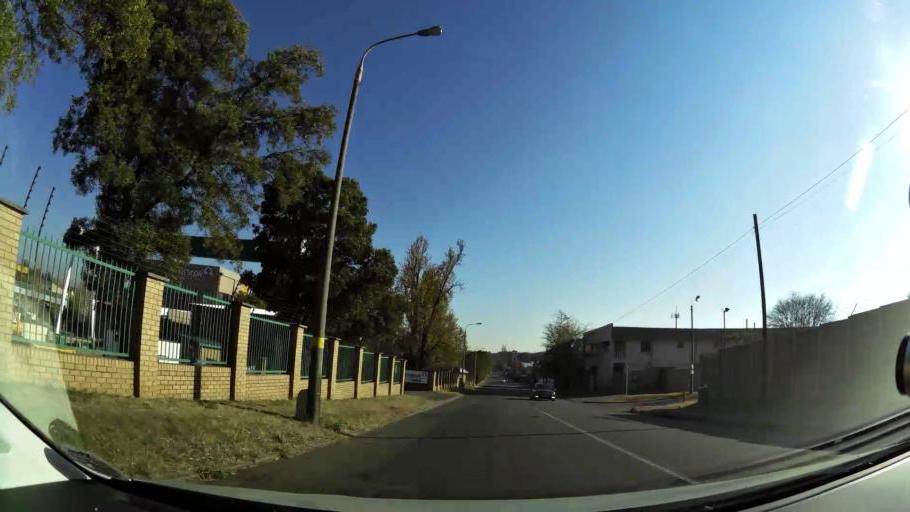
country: ZA
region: Gauteng
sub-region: City of Johannesburg Metropolitan Municipality
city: Modderfontein
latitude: -26.1362
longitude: 28.1636
